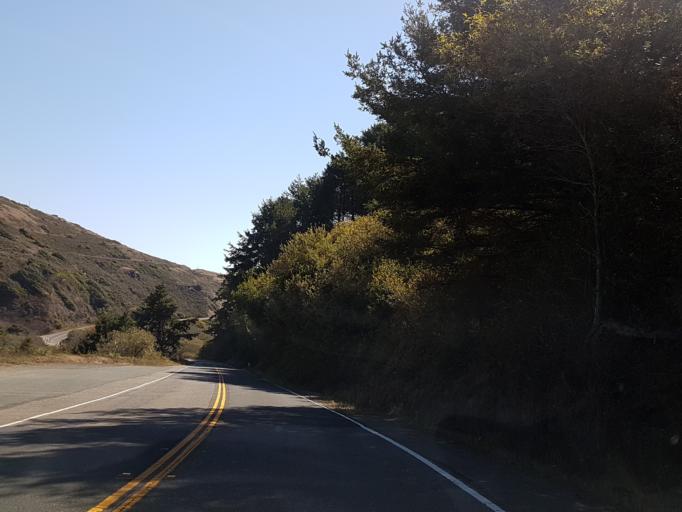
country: US
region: California
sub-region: Sonoma County
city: Monte Rio
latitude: 38.4735
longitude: -123.1556
